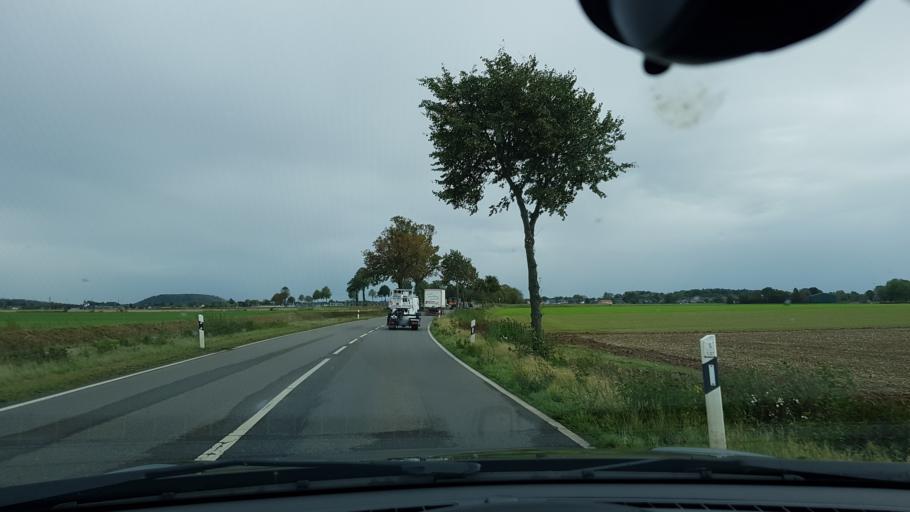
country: DE
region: North Rhine-Westphalia
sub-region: Regierungsbezirk Koln
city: Wassenberg
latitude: 51.0801
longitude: 6.1684
